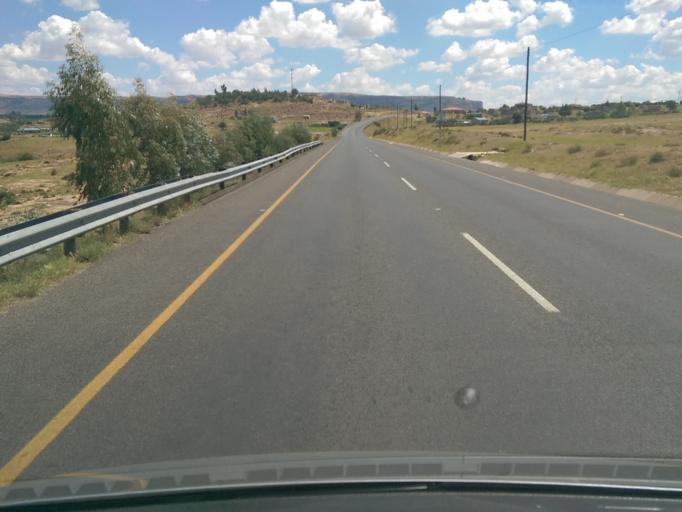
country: LS
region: Maseru
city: Maseru
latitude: -29.3948
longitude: 27.5264
